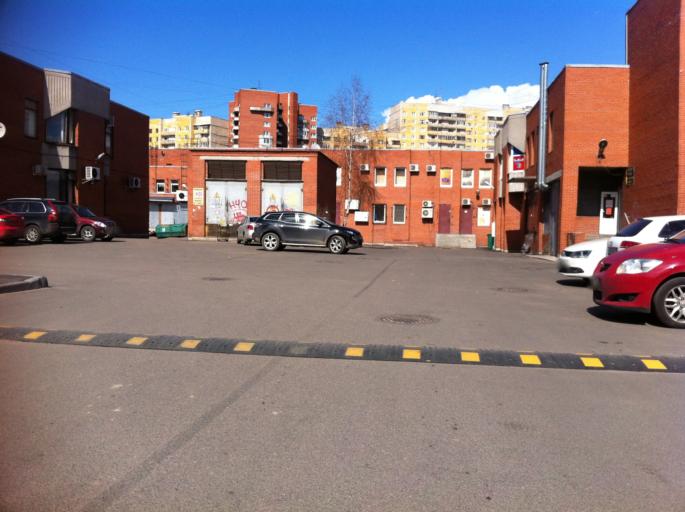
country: RU
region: St.-Petersburg
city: Uritsk
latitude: 59.8527
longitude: 30.1928
